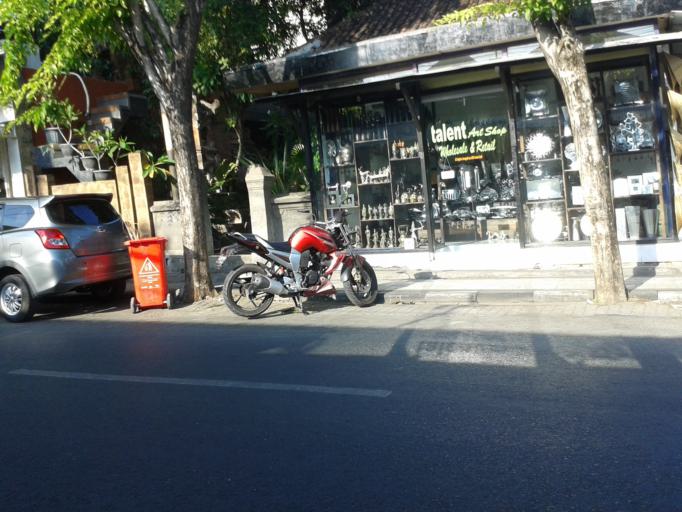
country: ID
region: Bali
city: Kuta
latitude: -8.7047
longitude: 115.1709
